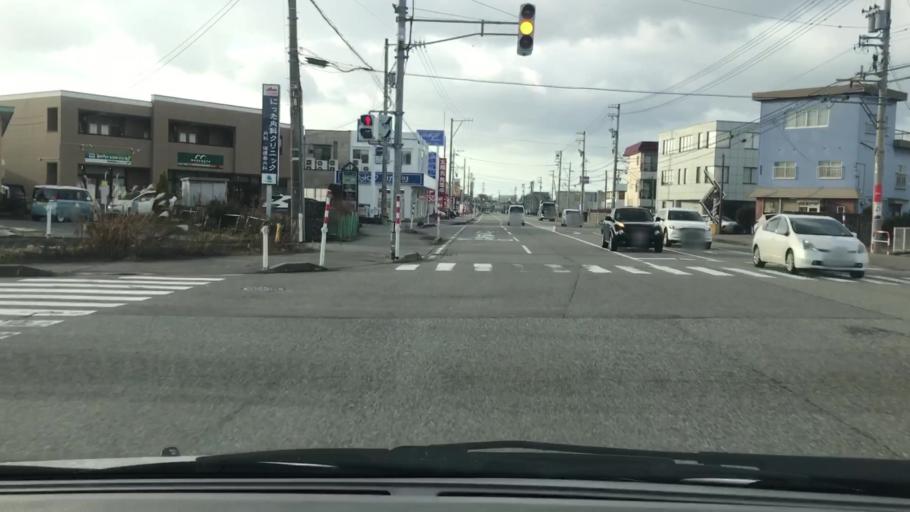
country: JP
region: Toyama
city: Toyama-shi
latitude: 36.6845
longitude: 137.2477
